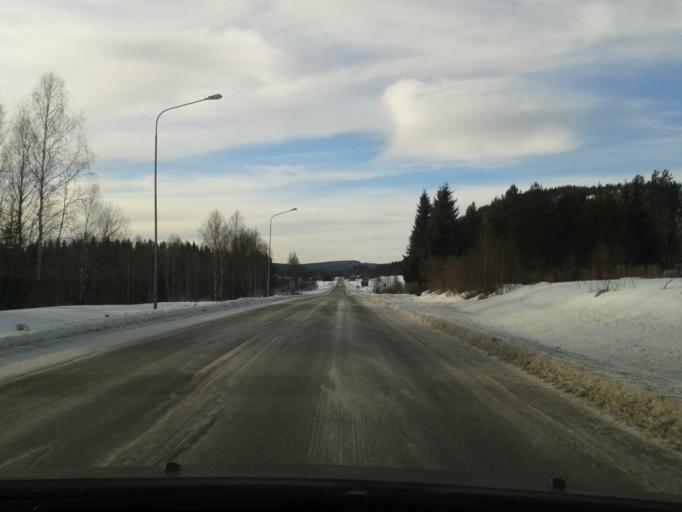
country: SE
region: Vaesternorrland
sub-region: OErnskoeldsviks Kommun
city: Bredbyn
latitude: 63.5265
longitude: 18.0262
